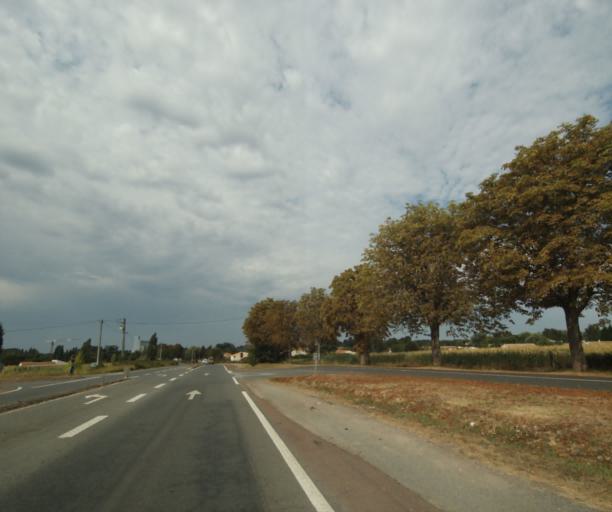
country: FR
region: Poitou-Charentes
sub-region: Departement de la Charente-Maritime
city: Cabariot
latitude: 45.9557
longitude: -0.8640
